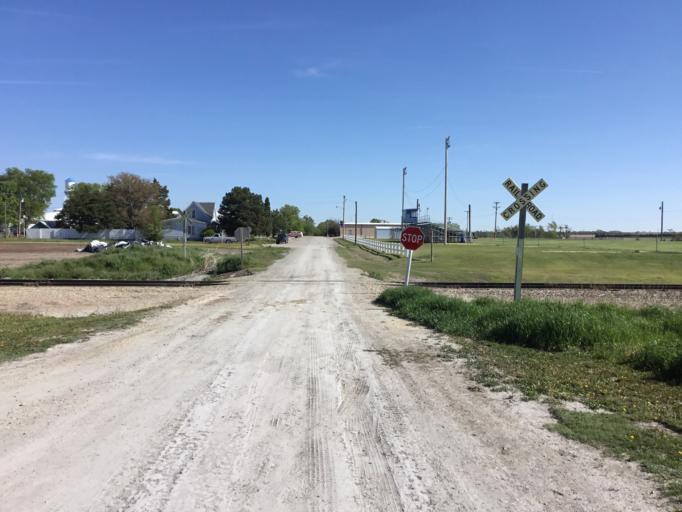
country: US
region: Kansas
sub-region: Smith County
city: Smith Center
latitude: 39.7634
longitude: -99.0292
